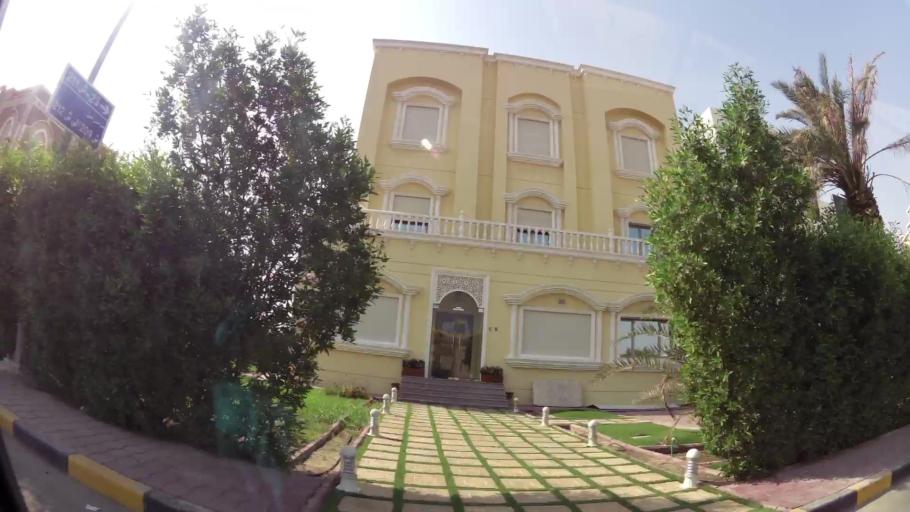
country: KW
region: Muhafazat al Jahra'
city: Al Jahra'
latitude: 29.3331
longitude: 47.7608
